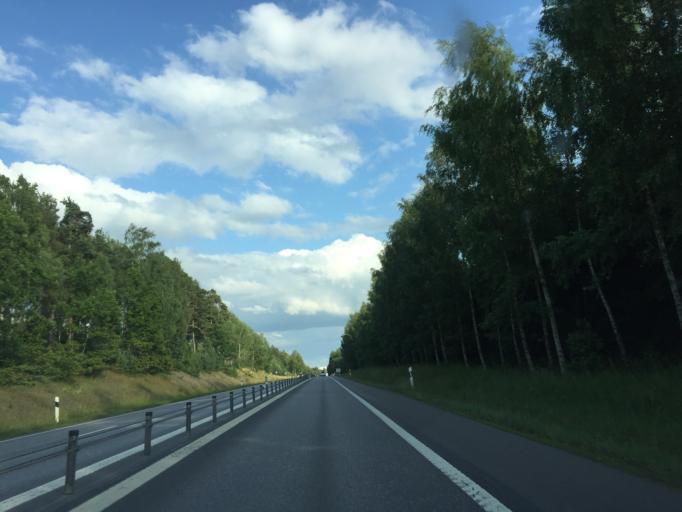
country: SE
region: OEstergoetland
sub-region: Motala Kommun
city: Motala
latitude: 58.5668
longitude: 14.9971
